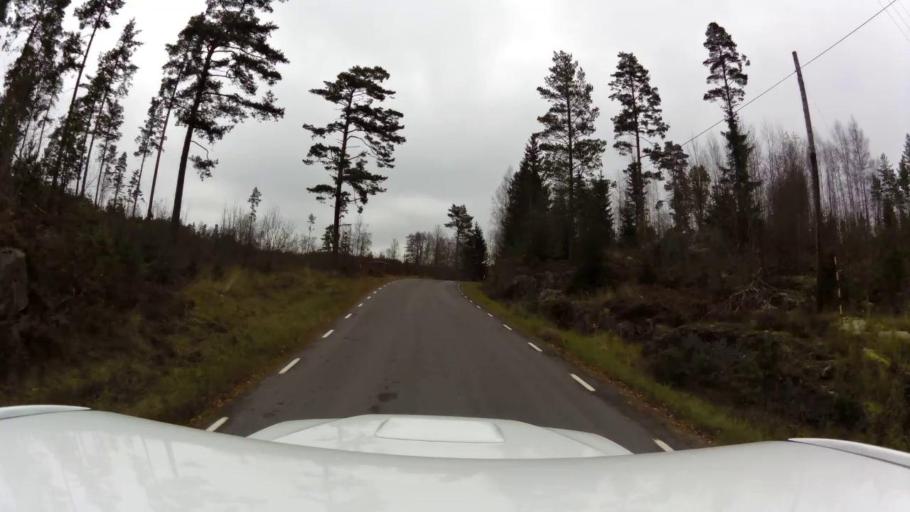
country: SE
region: OEstergoetland
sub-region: Kinda Kommun
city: Kisa
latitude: 58.1277
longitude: 15.4487
